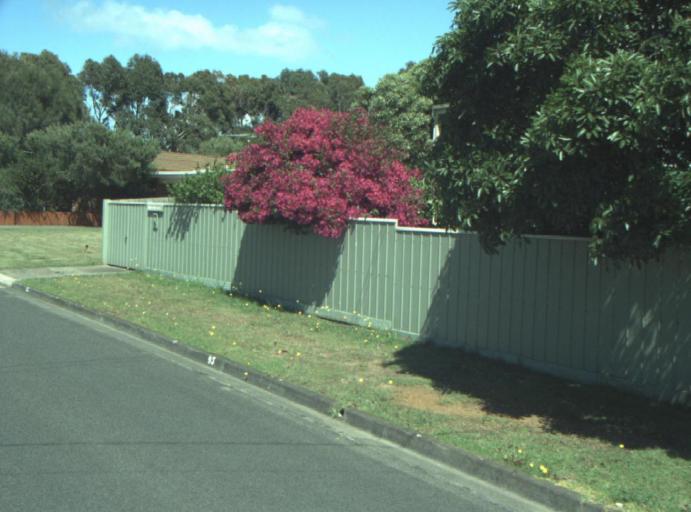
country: AU
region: Victoria
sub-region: Queenscliffe
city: Queenscliff
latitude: -38.1866
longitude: 144.7112
